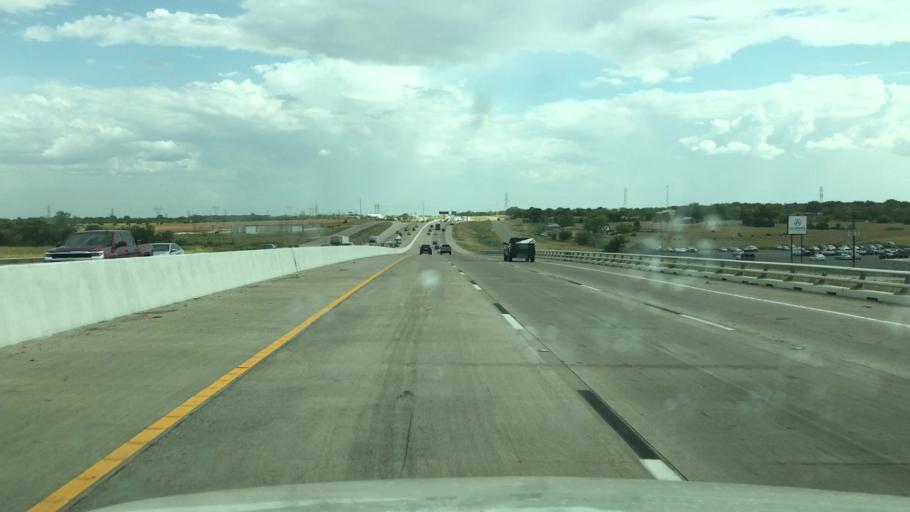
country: US
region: Texas
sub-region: McLennan County
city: Northcrest
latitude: 31.7144
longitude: -97.1025
